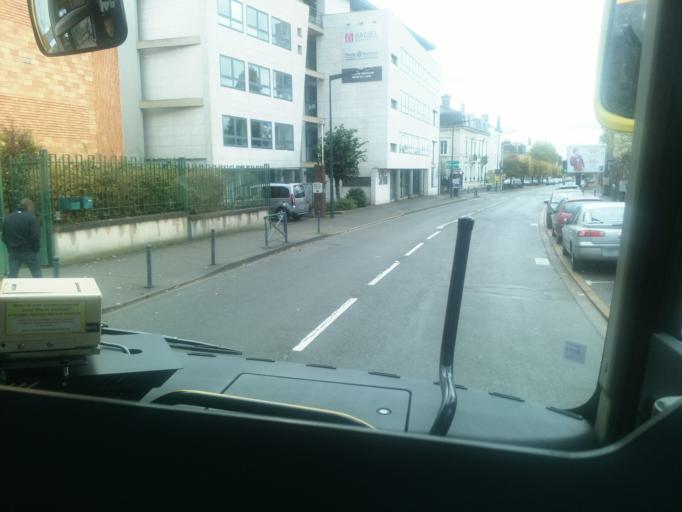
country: FR
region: Centre
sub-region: Departement d'Eure-et-Loir
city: Chartres
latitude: 48.4402
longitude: 1.4824
